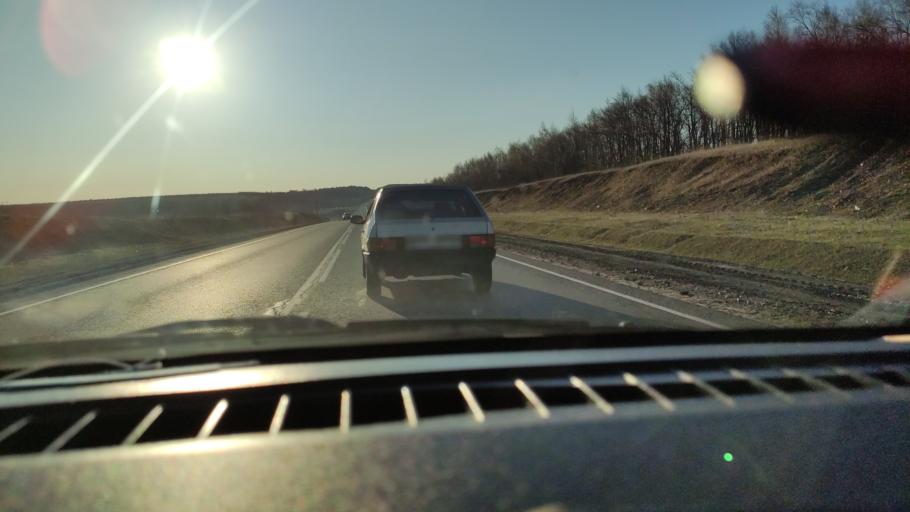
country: RU
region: Saratov
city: Shikhany
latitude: 52.1161
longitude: 47.2886
